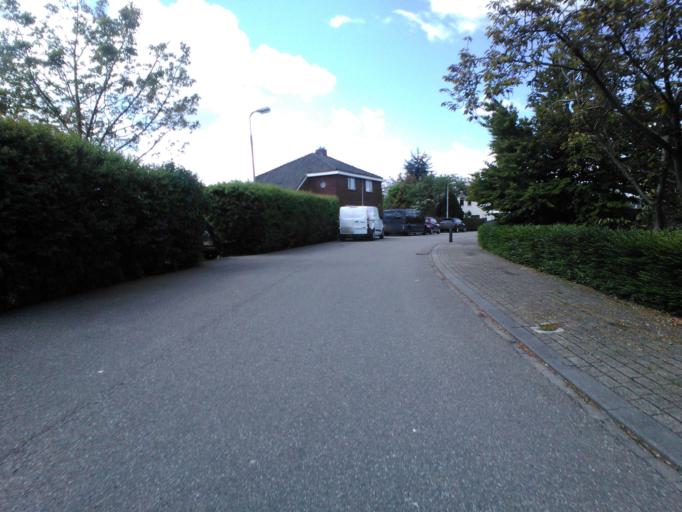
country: NL
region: South Holland
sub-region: Gemeente Hendrik-Ido-Ambacht
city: Hendrik-Ido-Ambacht
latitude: 51.8520
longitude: 4.6336
